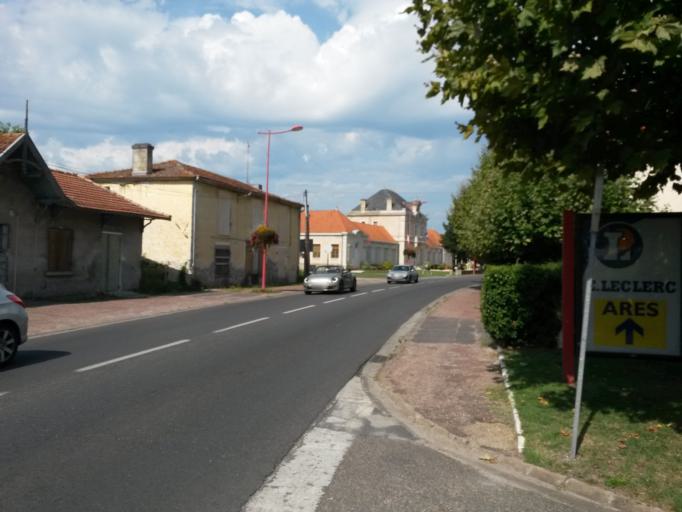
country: FR
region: Aquitaine
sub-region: Departement de la Gironde
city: Lanton
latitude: 44.7019
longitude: -1.0342
